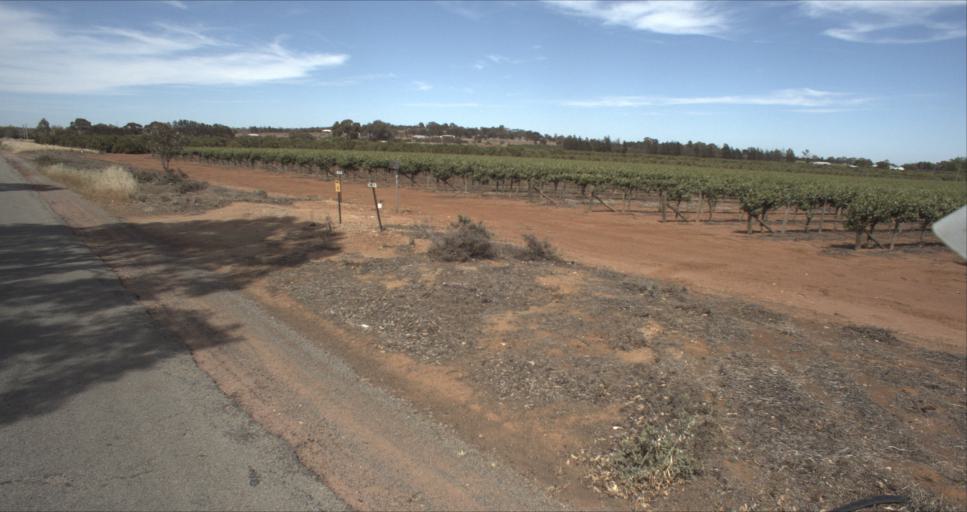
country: AU
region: New South Wales
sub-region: Leeton
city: Leeton
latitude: -34.5669
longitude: 146.4561
